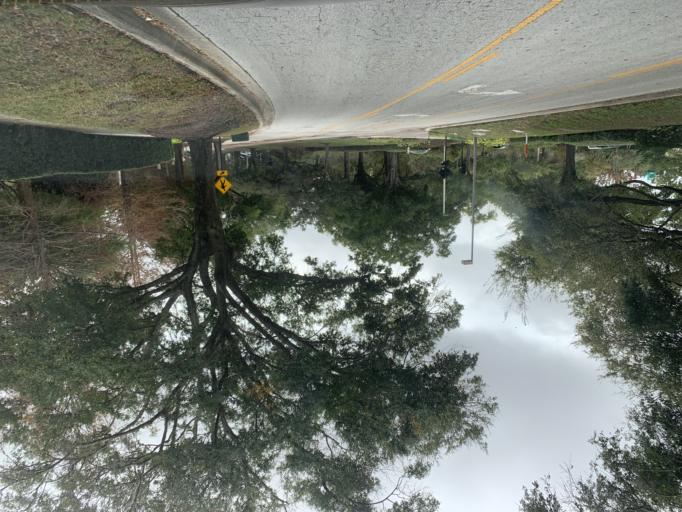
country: US
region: Florida
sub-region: Orange County
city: Eatonville
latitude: 28.6290
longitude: -81.3957
